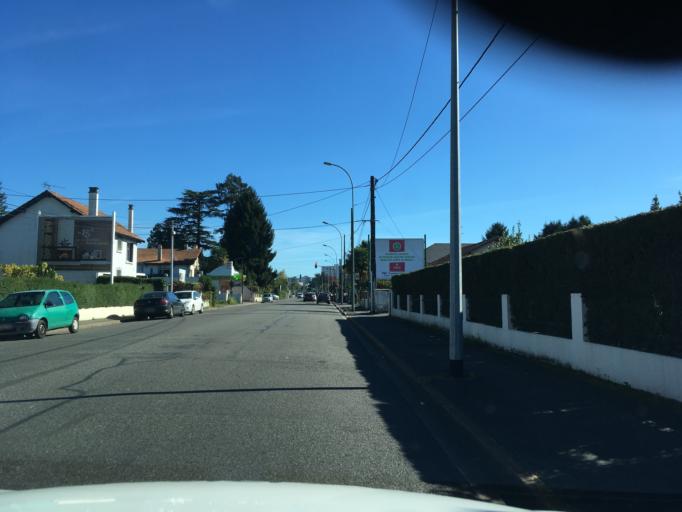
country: FR
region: Aquitaine
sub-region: Departement des Pyrenees-Atlantiques
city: Lons
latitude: 43.3241
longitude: -0.3759
